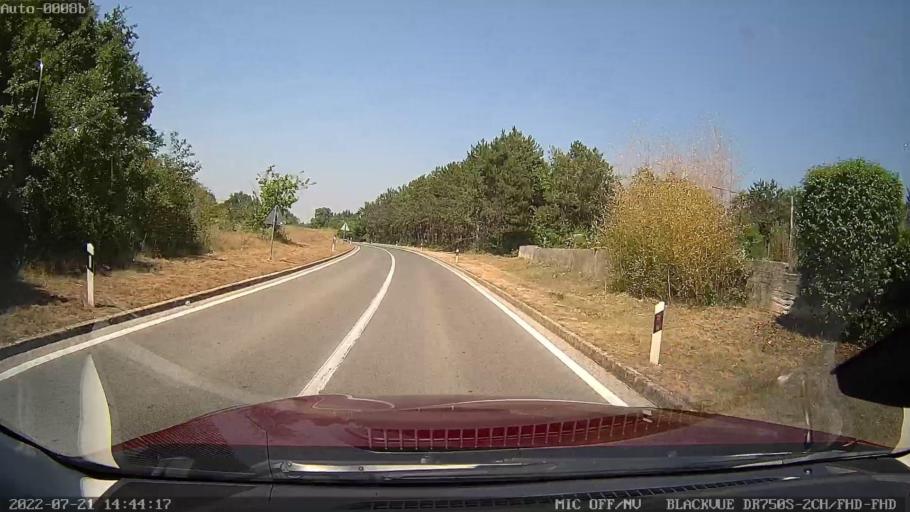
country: HR
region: Istarska
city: Pazin
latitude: 45.1161
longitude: 13.8844
